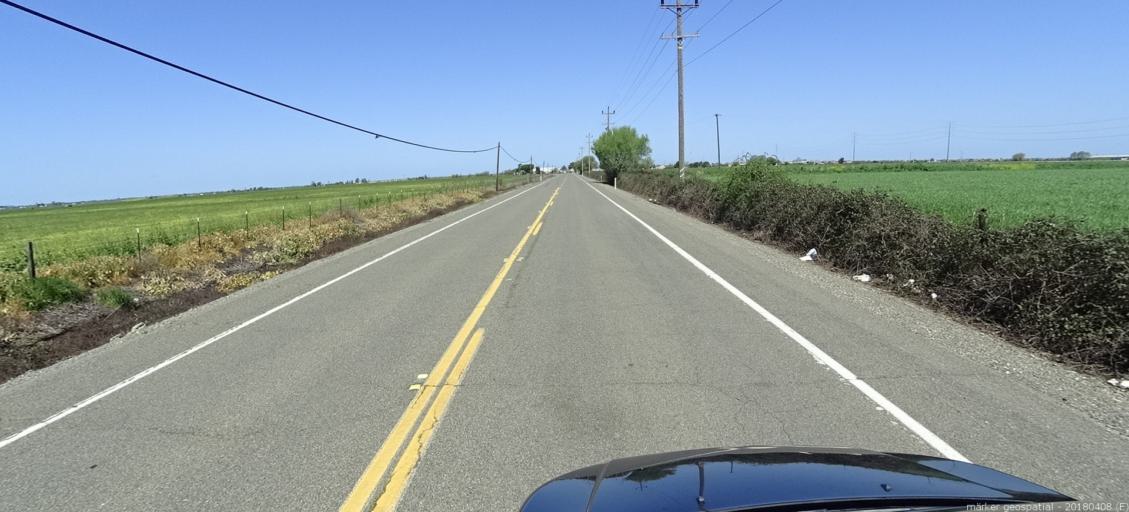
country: US
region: California
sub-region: Sacramento County
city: Laguna
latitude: 38.3582
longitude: -121.4524
